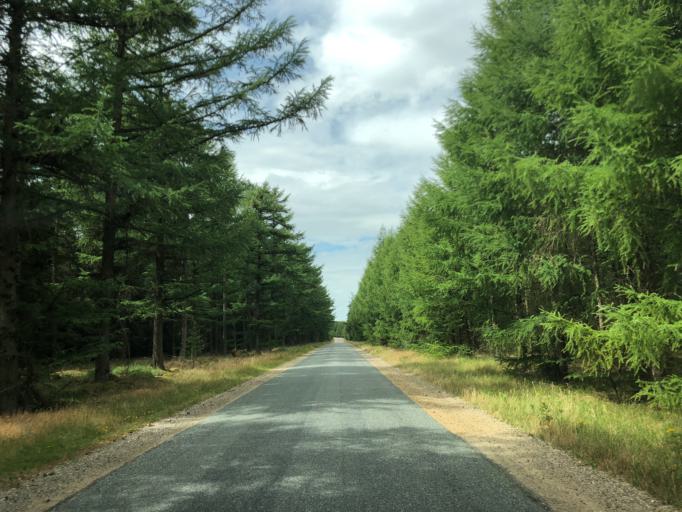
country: DK
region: South Denmark
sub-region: Billund Kommune
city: Grindsted
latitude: 55.6481
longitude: 8.8931
